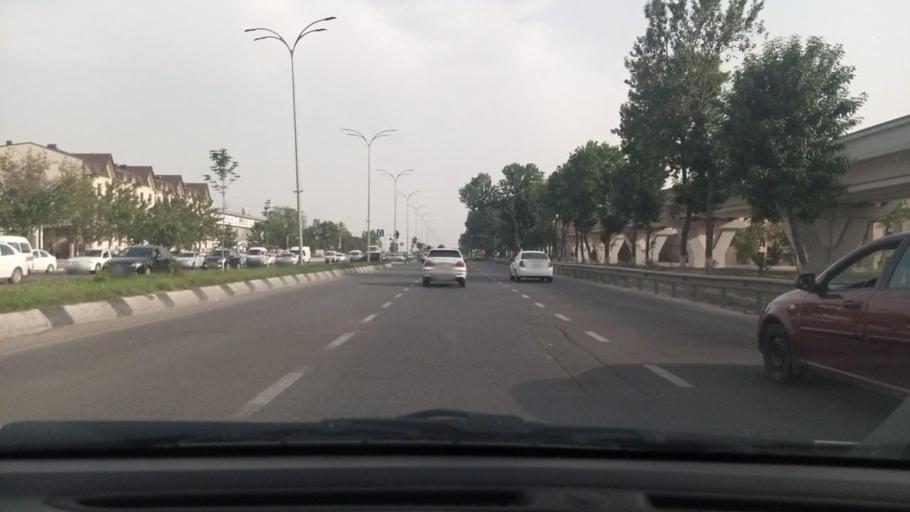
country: UZ
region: Toshkent Shahri
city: Bektemir
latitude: 41.2876
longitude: 69.3597
